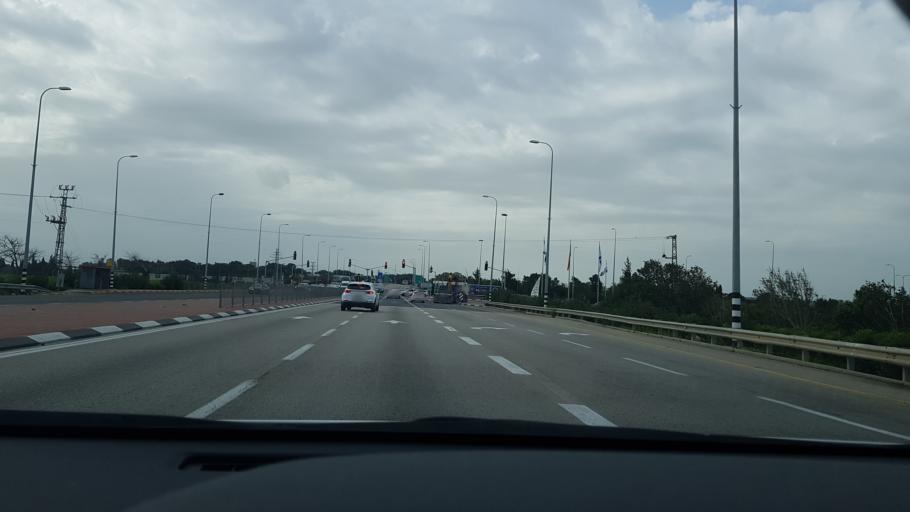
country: IL
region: Southern District
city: Ashqelon
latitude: 31.6818
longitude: 34.6096
